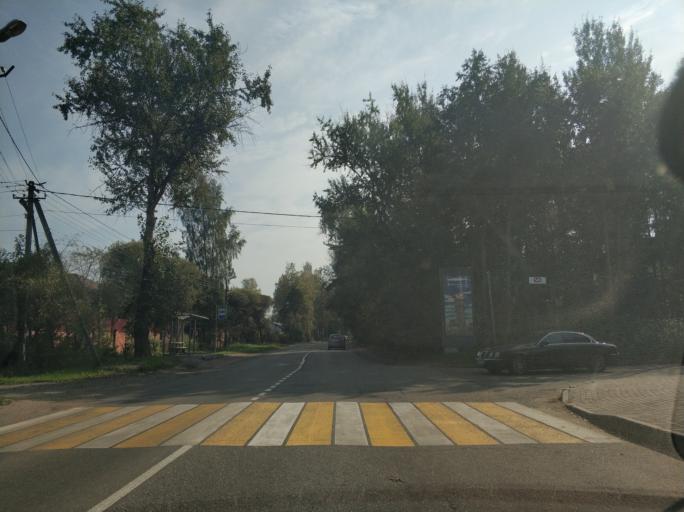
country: RU
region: Leningrad
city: Yanino Vtoroye
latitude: 60.0118
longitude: 30.5932
